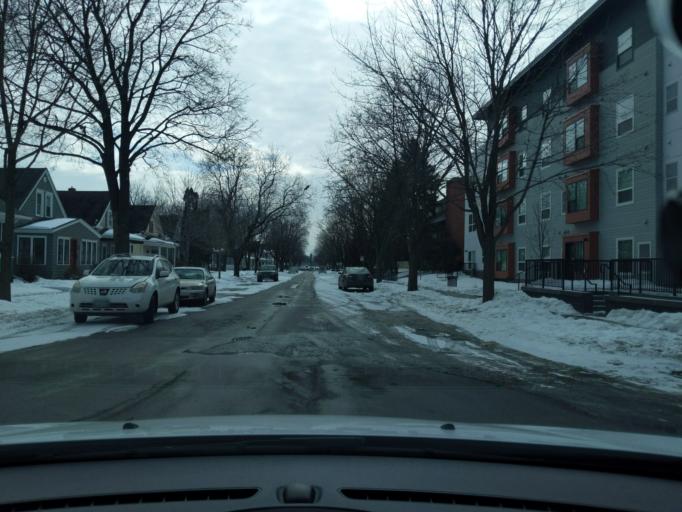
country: US
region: Minnesota
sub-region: Ramsey County
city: Falcon Heights
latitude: 44.9593
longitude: -93.1638
